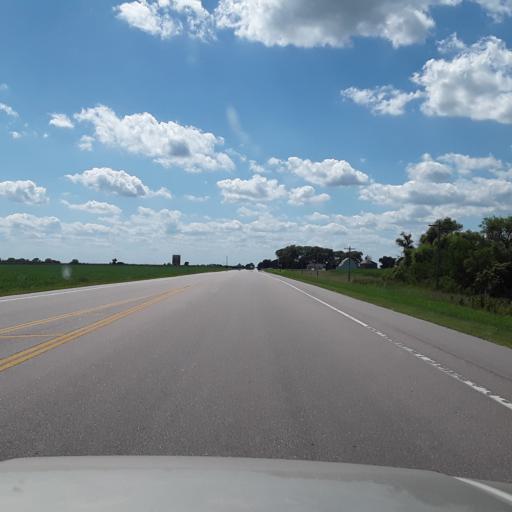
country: US
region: Nebraska
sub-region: Merrick County
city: Central City
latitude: 41.1910
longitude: -97.9847
